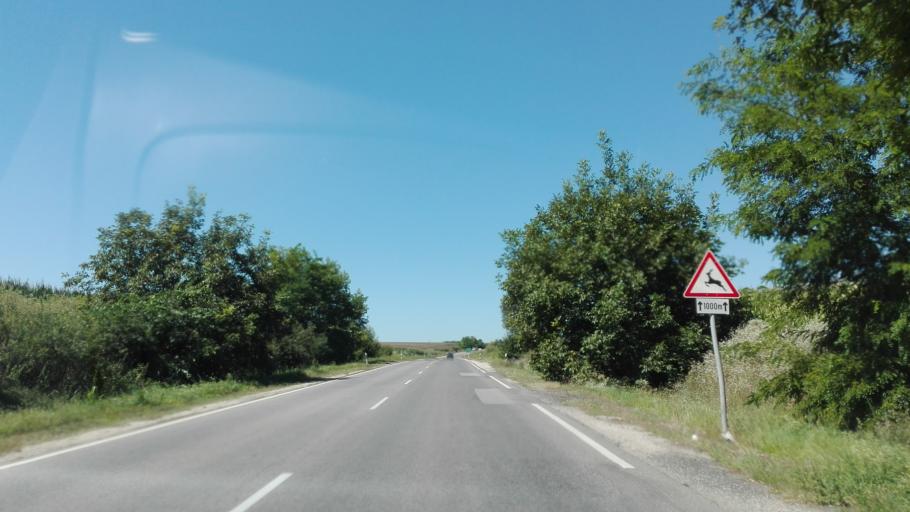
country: HU
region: Fejer
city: Mezoszilas
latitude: 46.8315
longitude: 18.4647
